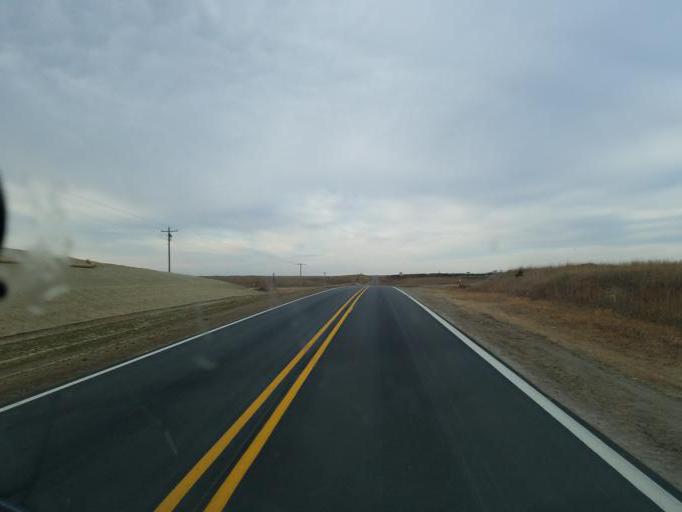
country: US
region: Nebraska
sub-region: Knox County
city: Center
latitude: 42.5970
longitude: -97.7787
